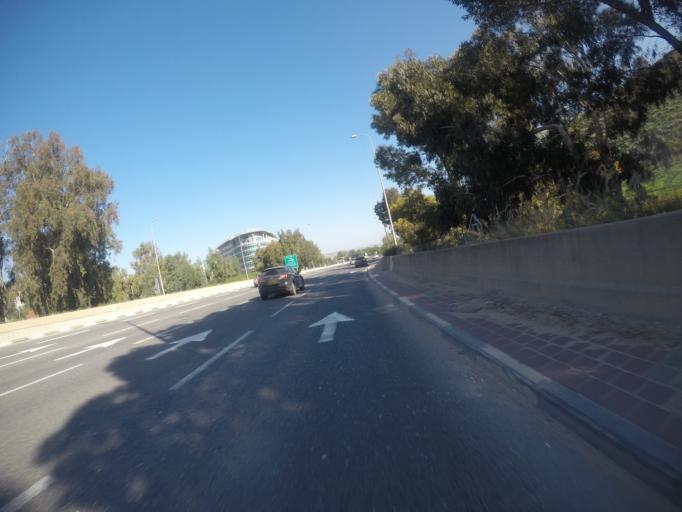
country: IL
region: Haifa
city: Daliyat el Karmil
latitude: 32.6648
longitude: 35.1068
